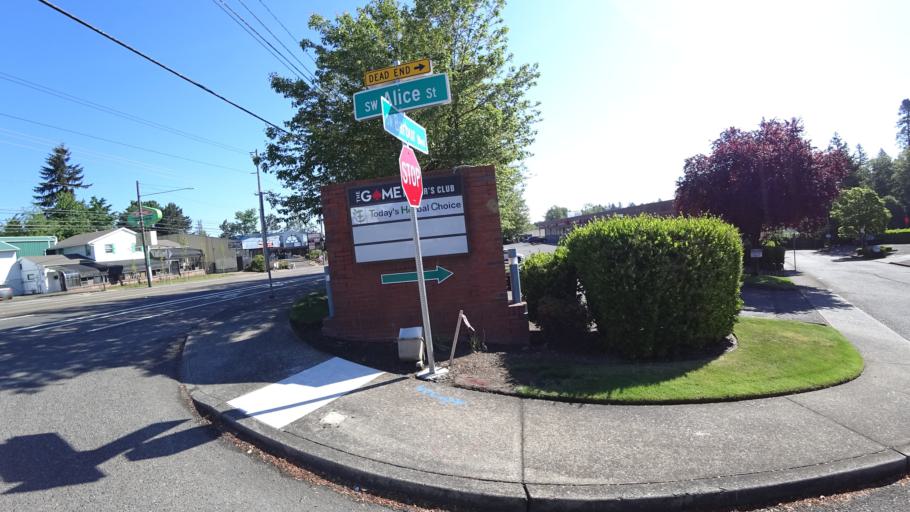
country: US
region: Oregon
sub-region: Washington County
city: Garden Home-Whitford
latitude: 45.4584
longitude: -122.7099
